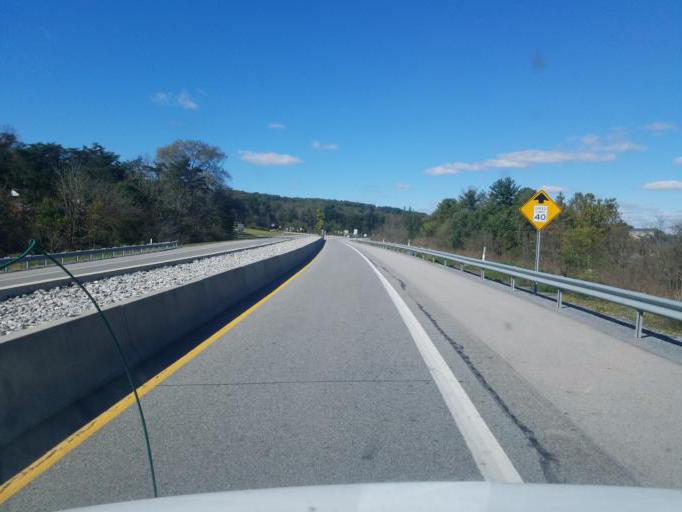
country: US
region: Pennsylvania
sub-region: Bedford County
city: Bedford
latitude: 40.0354
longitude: -78.5197
